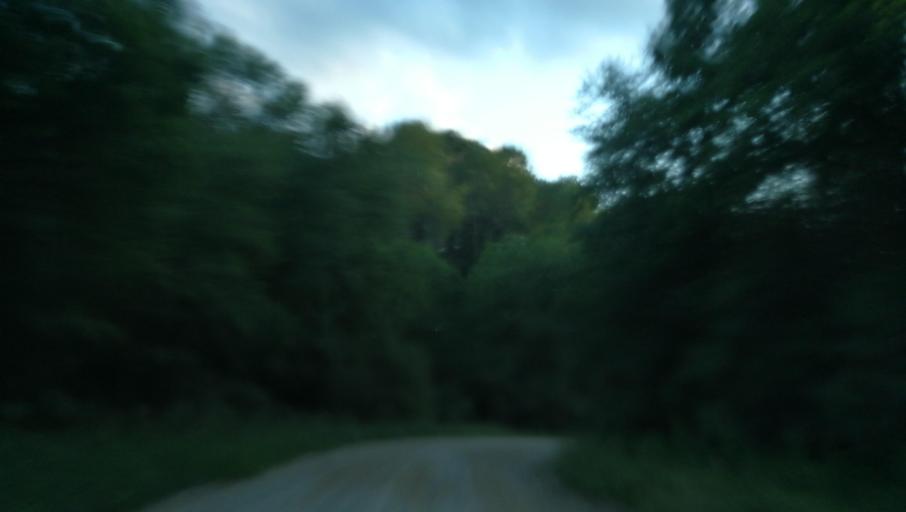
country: LV
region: Ligatne
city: Ligatne
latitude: 57.2602
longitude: 25.1525
